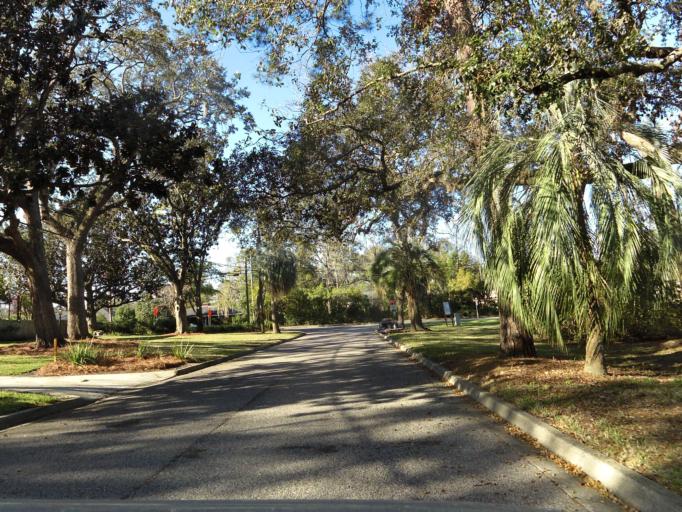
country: US
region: Florida
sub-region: Duval County
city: Jacksonville
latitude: 30.3023
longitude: -81.6504
